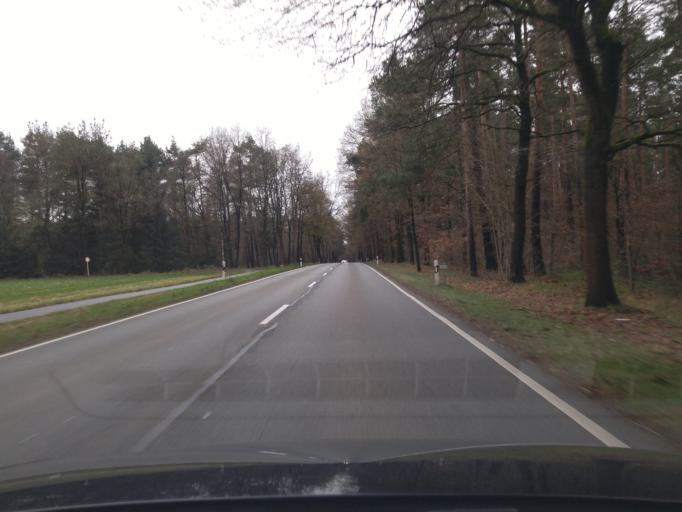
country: DE
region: Lower Saxony
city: Winsen
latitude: 52.7267
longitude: 9.9262
